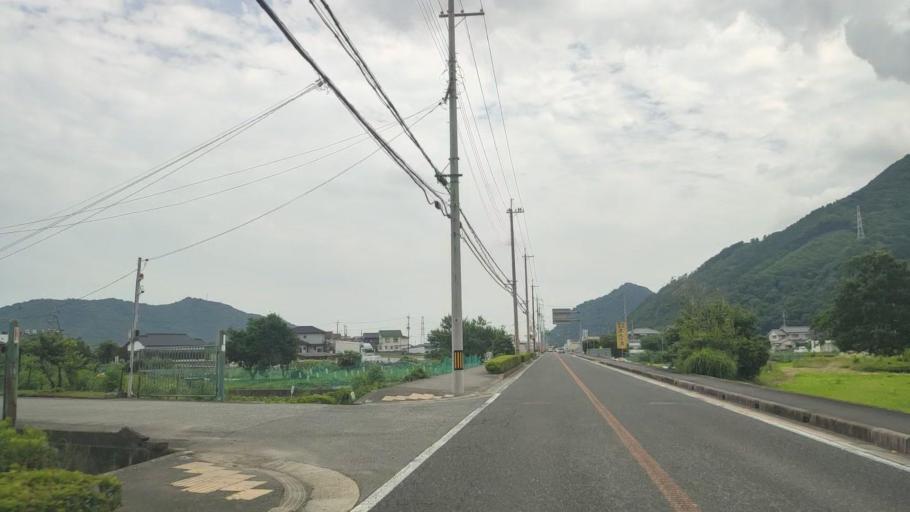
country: JP
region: Hyogo
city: Tatsunocho-tominaga
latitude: 34.8921
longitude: 134.5464
